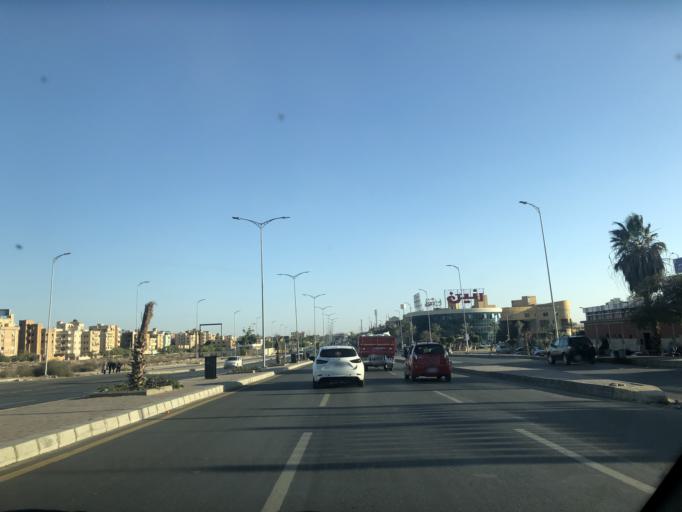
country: EG
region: Al Jizah
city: Madinat Sittah Uktubar
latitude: 29.9504
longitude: 30.9125
